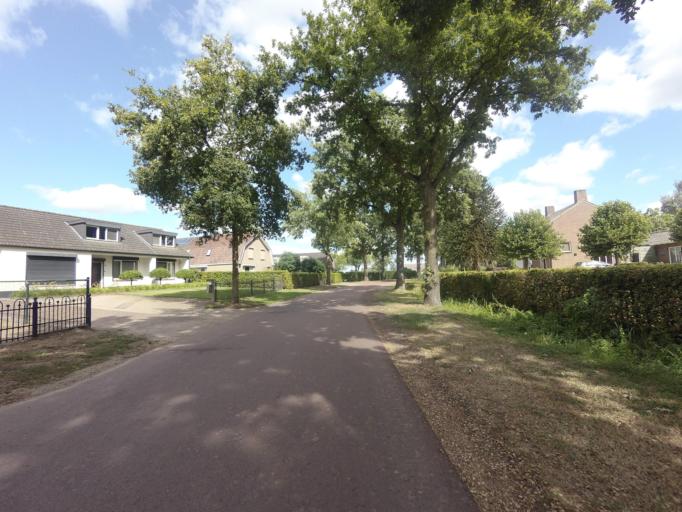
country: NL
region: North Brabant
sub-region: Gemeente Oss
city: Berghem
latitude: 51.7780
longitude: 5.5952
